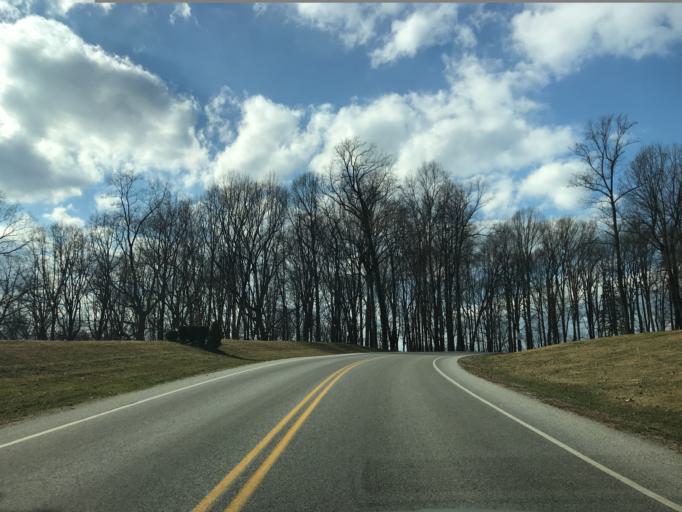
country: US
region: Pennsylvania
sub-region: Chester County
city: Oxford
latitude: 39.7468
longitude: -76.0220
